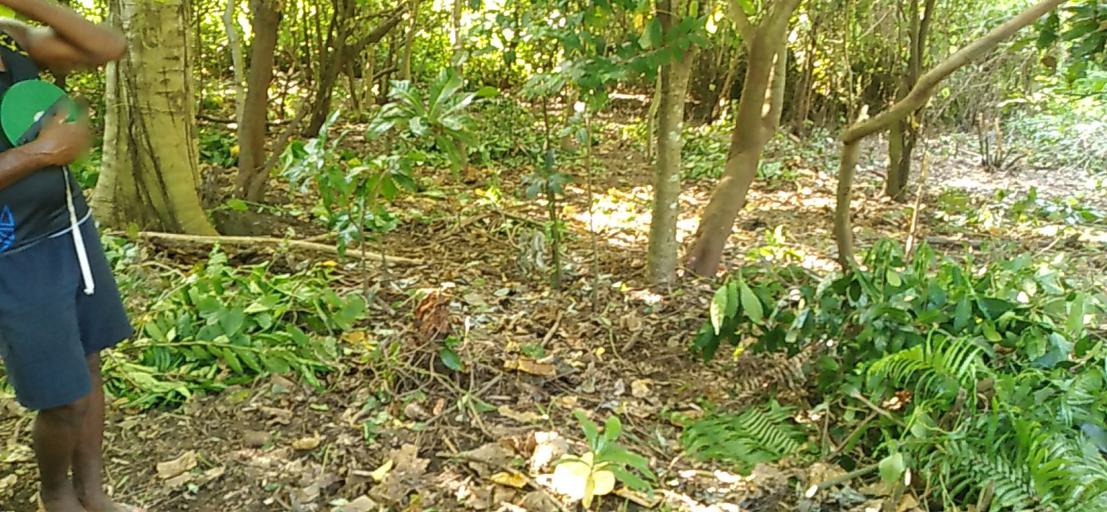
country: VU
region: Penama
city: Saratamata
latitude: -15.2871
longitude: 167.9100
